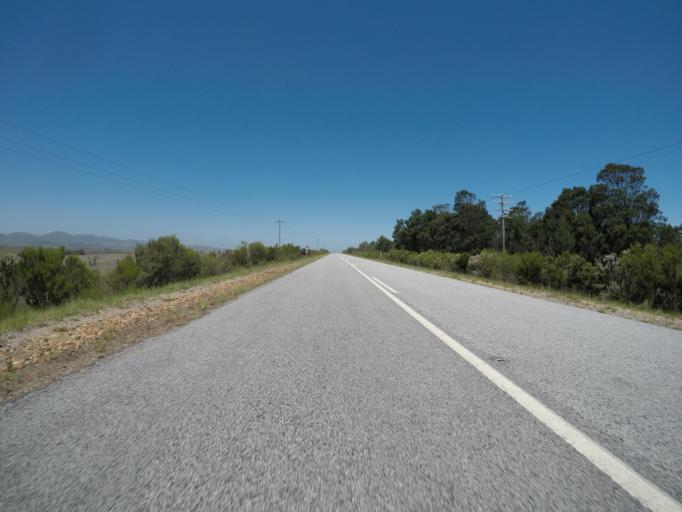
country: ZA
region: Eastern Cape
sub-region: Cacadu District Municipality
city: Kareedouw
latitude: -33.9800
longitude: 24.5027
